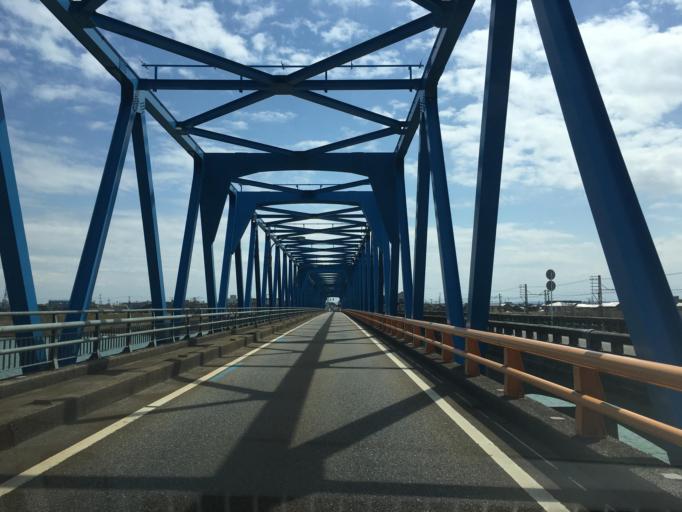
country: JP
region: Toyama
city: Nishishinminato
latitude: 36.7870
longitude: 137.0692
